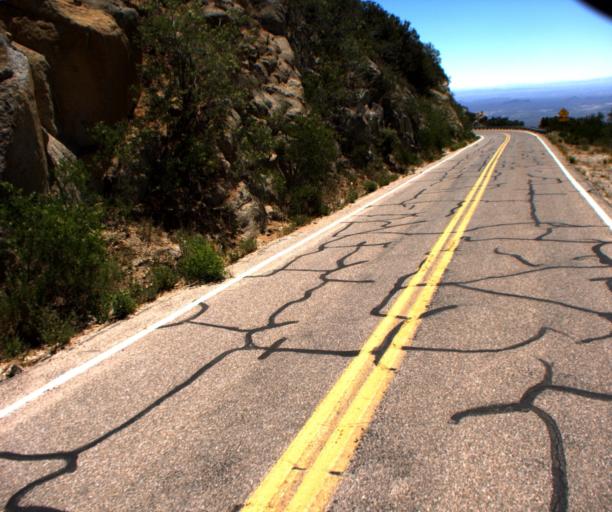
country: US
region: Arizona
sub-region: Pima County
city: Sells
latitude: 31.9653
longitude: -111.6000
